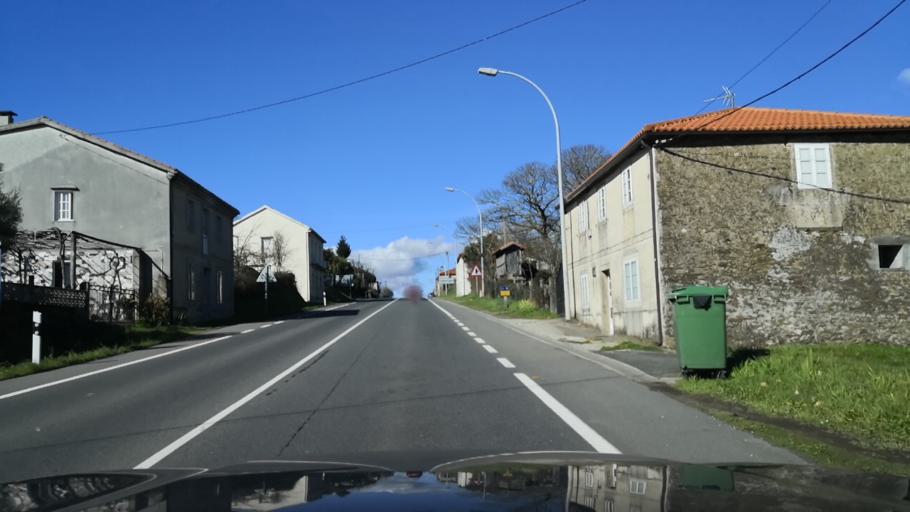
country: ES
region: Galicia
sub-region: Provincia de Pontevedra
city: Lalin
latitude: 42.6770
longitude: -8.1652
